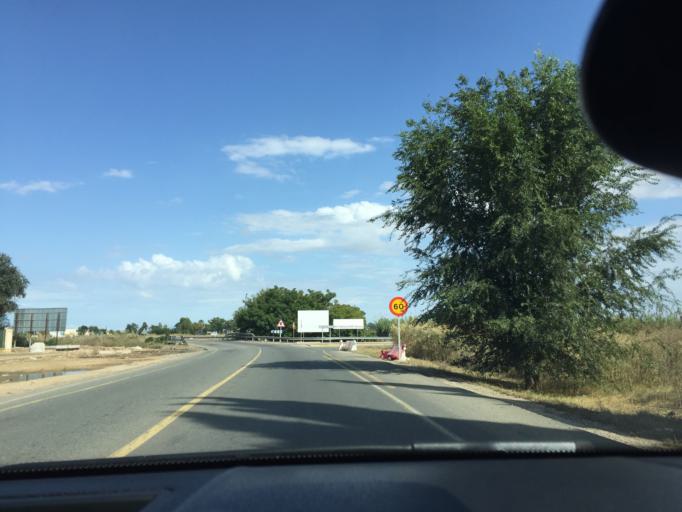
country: ES
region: Andalusia
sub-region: Provincia de Sevilla
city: Coria del Rio
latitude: 37.3019
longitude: -6.0430
